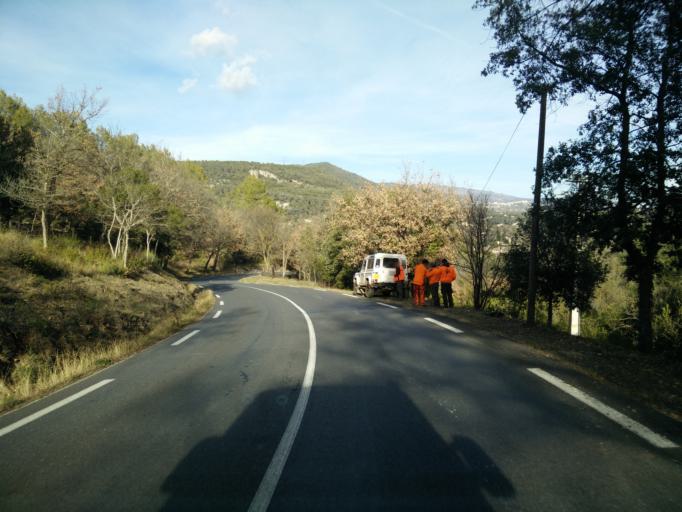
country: FR
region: Provence-Alpes-Cote d'Azur
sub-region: Departement des Alpes-Maritimes
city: Le Tignet
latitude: 43.6167
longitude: 6.8222
